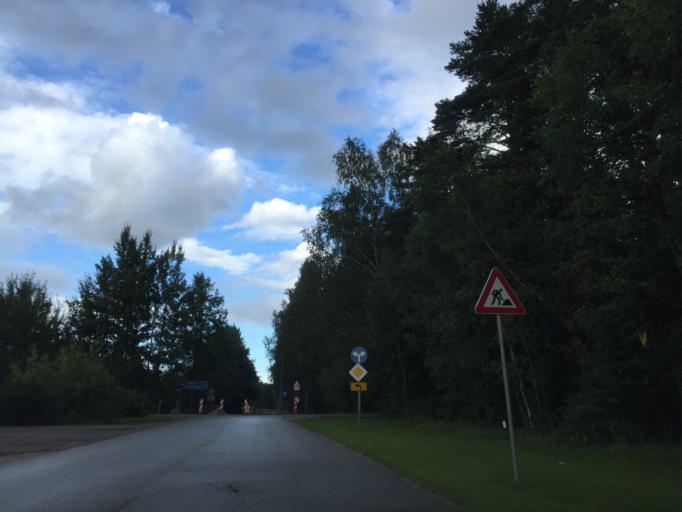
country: LV
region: Babite
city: Pinki
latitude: 56.9529
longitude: 23.9523
